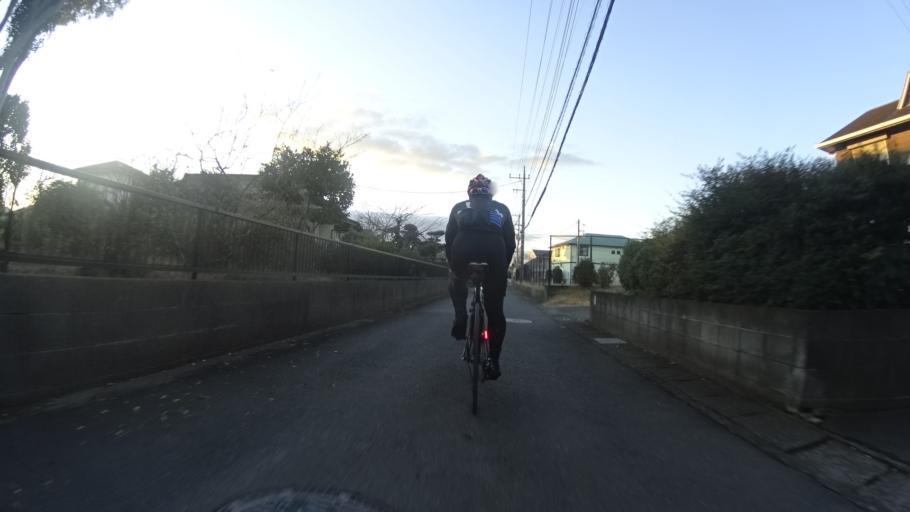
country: JP
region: Kanagawa
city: Zama
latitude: 35.5166
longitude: 139.3683
